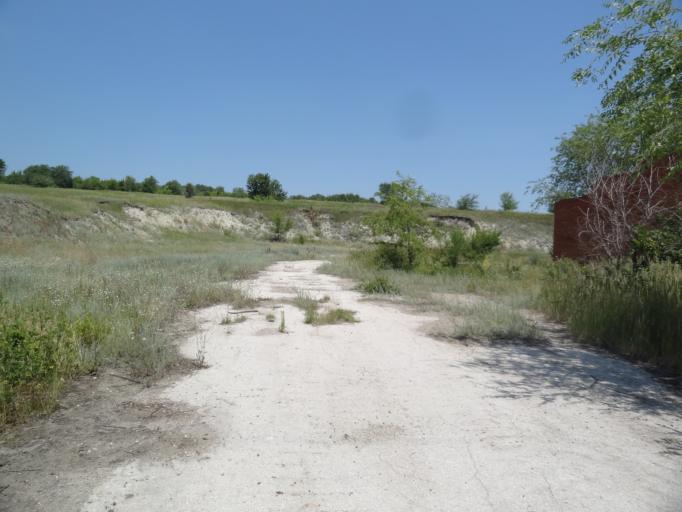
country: RU
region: Saratov
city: Sokolovyy
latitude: 51.4206
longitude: 45.8168
